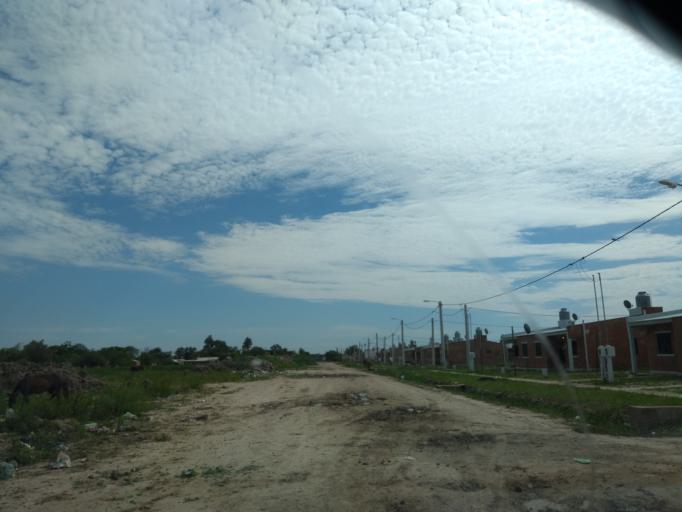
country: AR
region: Chaco
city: Fontana
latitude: -27.3971
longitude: -58.9855
